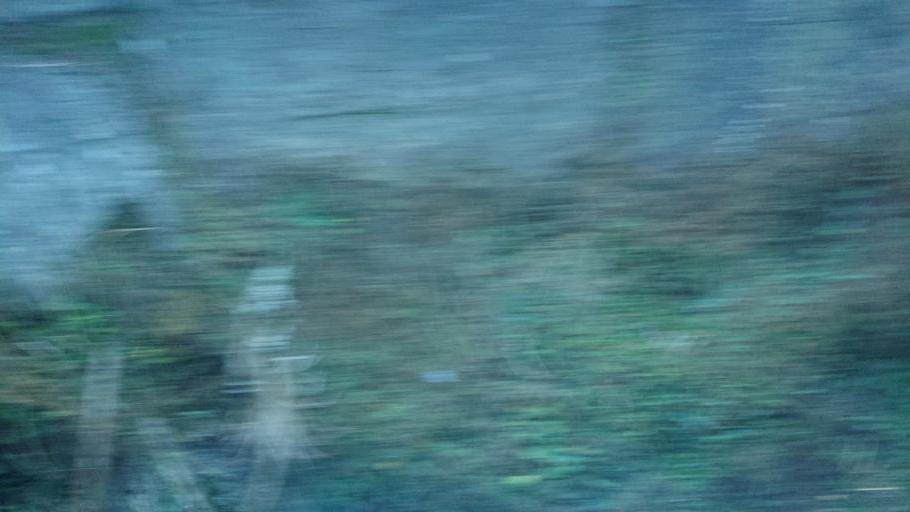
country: TW
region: Taiwan
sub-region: Chiayi
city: Jiayi Shi
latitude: 23.5187
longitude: 120.6283
